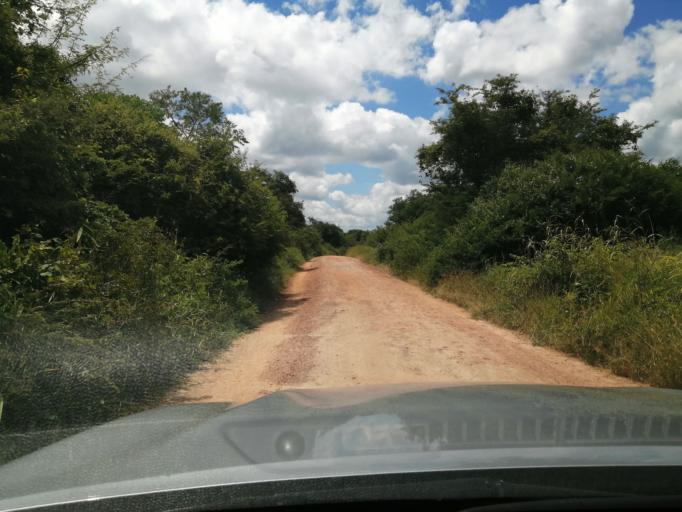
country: ZM
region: Lusaka
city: Lusaka
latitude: -15.1324
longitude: 27.9113
